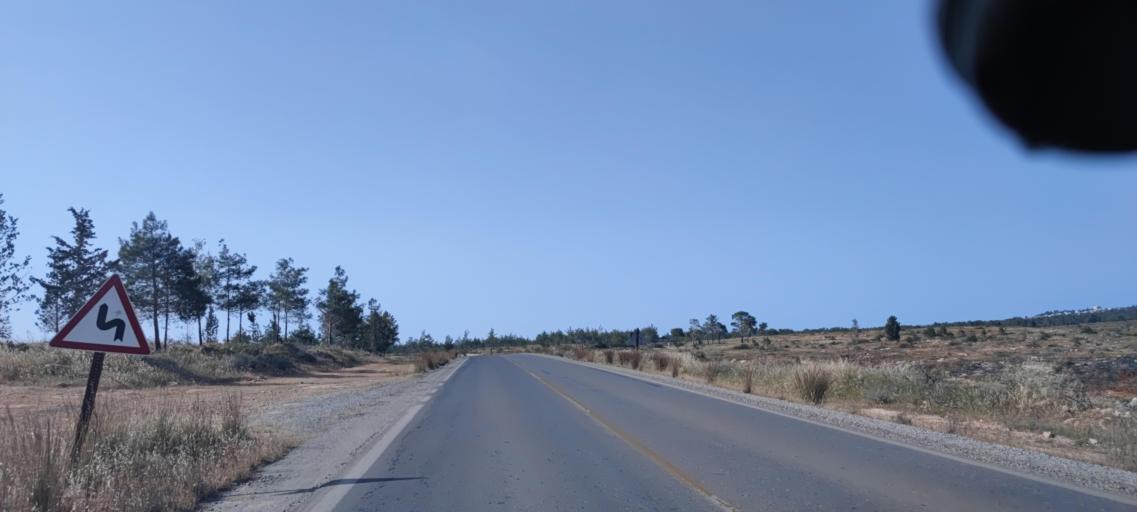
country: CY
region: Lefkosia
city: Morfou
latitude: 35.2783
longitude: 33.0412
